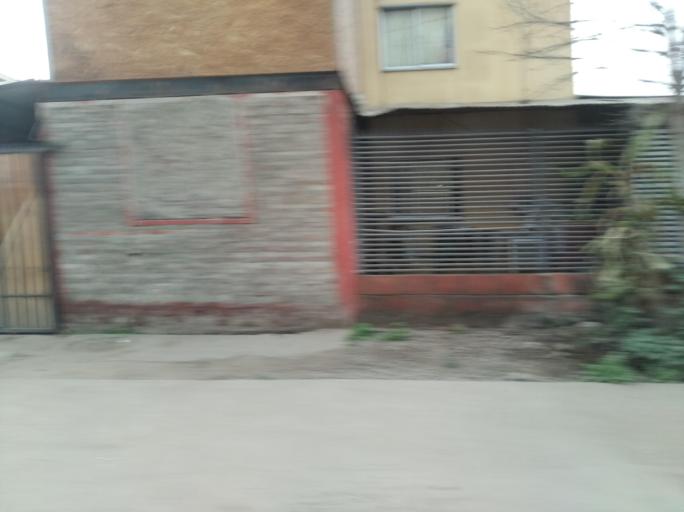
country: CL
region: Santiago Metropolitan
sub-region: Provincia de Chacabuco
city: Lampa
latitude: -33.2874
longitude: -70.8870
